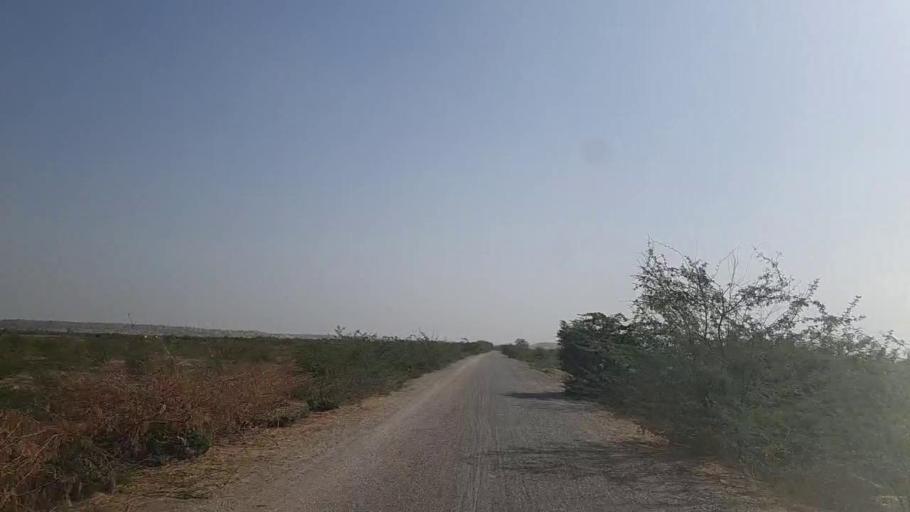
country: PK
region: Sindh
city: Kadhan
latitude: 24.5663
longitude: 69.2764
